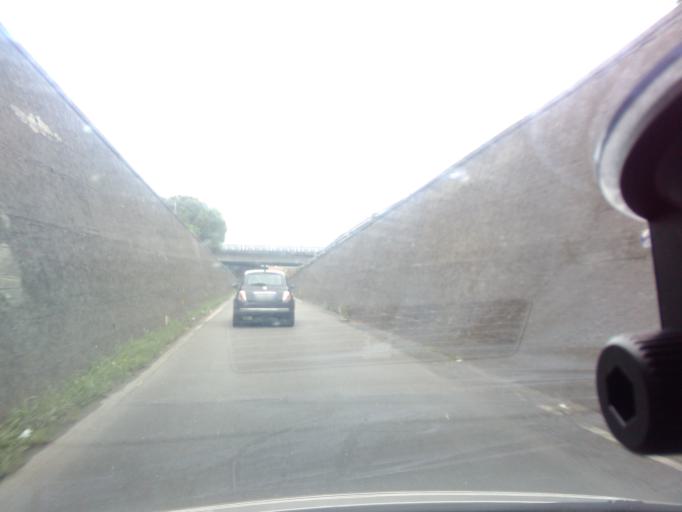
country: IT
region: Tuscany
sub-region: Provincia di Massa-Carrara
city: Massa
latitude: 44.0203
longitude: 10.1145
